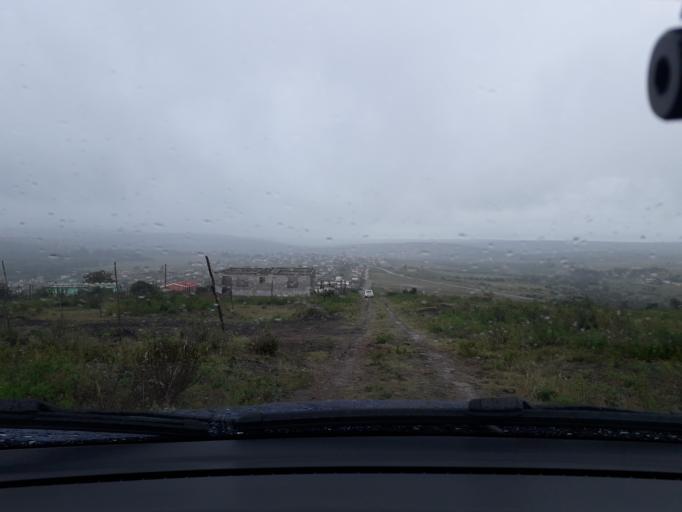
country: ZA
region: Eastern Cape
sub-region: Buffalo City Metropolitan Municipality
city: Bhisho
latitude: -32.8029
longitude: 27.3627
